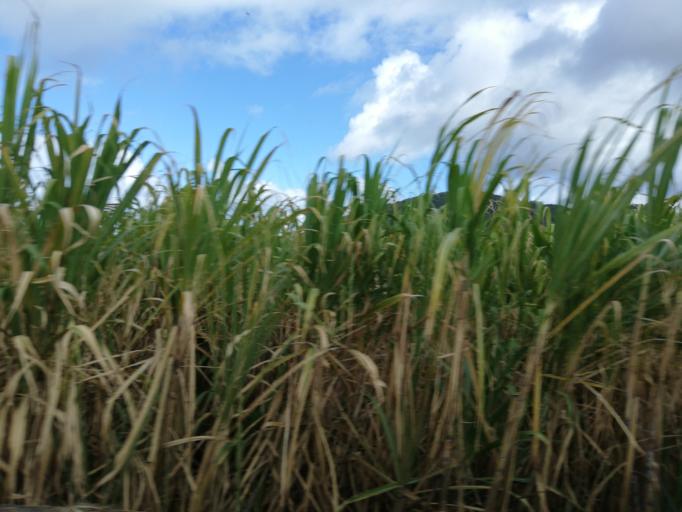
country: MU
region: Flacq
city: Grande Riviere Sud Est
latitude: -20.2746
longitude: 57.7673
